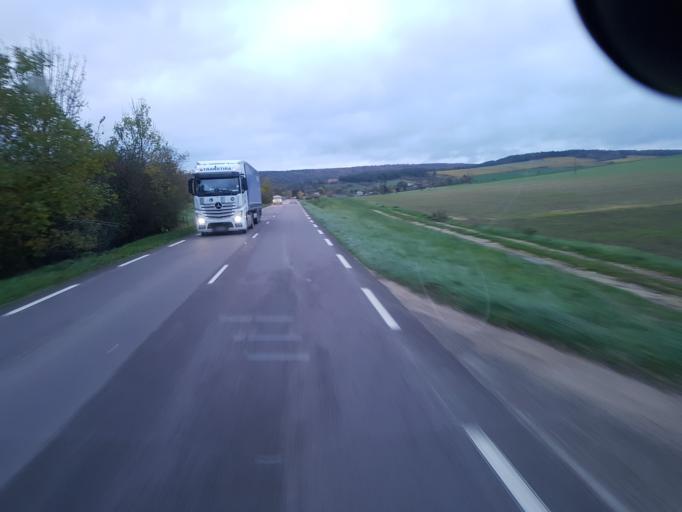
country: FR
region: Champagne-Ardenne
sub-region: Departement de l'Aube
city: Mussy-sur-Seine
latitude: 47.9661
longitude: 4.4996
